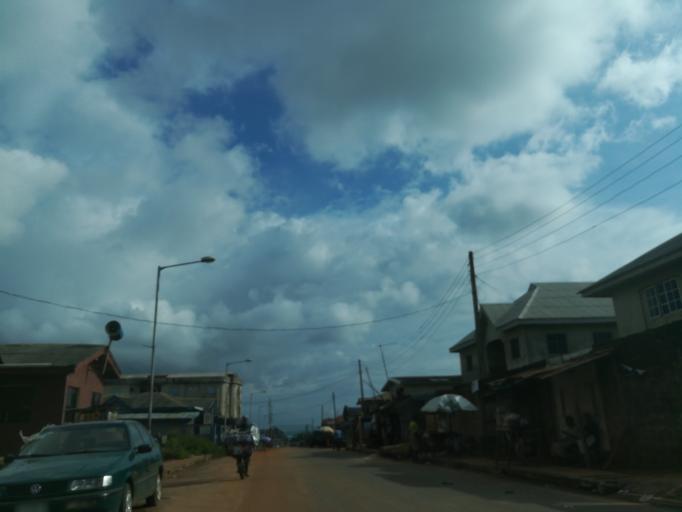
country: NG
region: Lagos
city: Ikorodu
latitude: 6.6003
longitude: 3.5056
